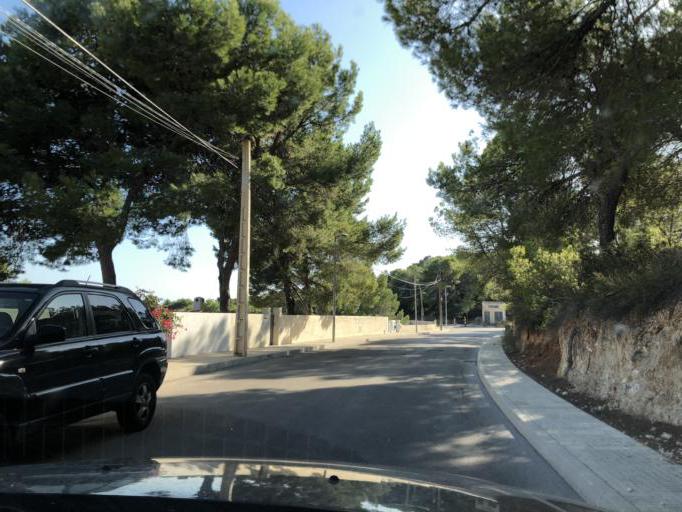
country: ES
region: Balearic Islands
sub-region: Illes Balears
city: Camp de Mar
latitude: 39.5422
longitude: 2.4073
